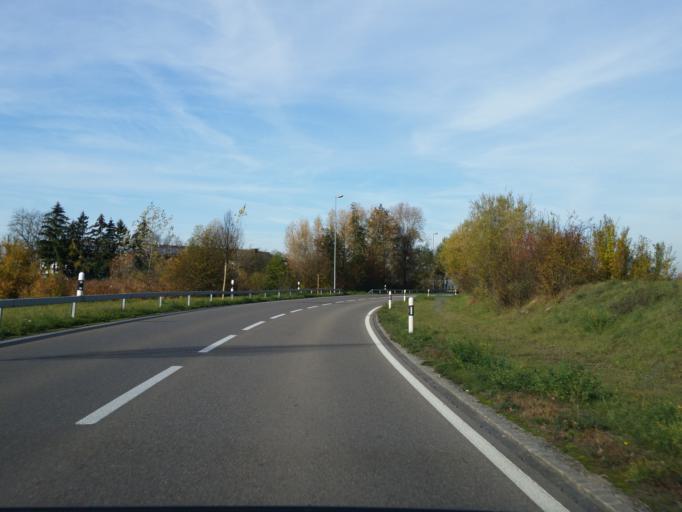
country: CH
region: Thurgau
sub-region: Kreuzlingen District
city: Gottlieben
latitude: 47.6576
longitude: 9.1477
